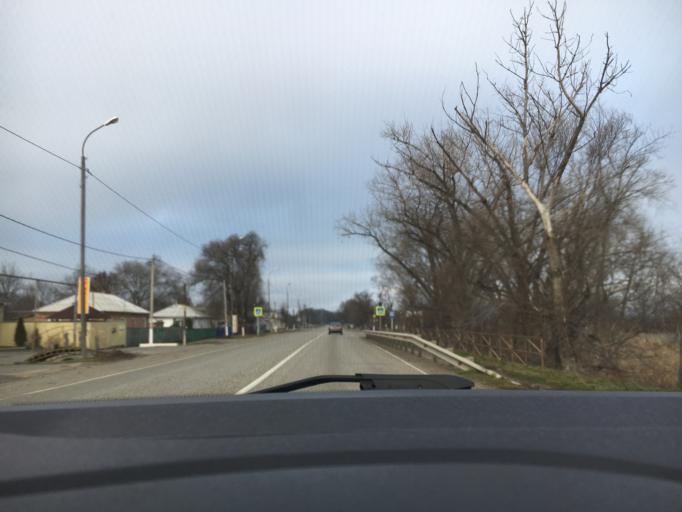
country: RU
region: Stavropol'skiy
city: Novoaleksandrovsk
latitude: 45.4518
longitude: 41.3156
